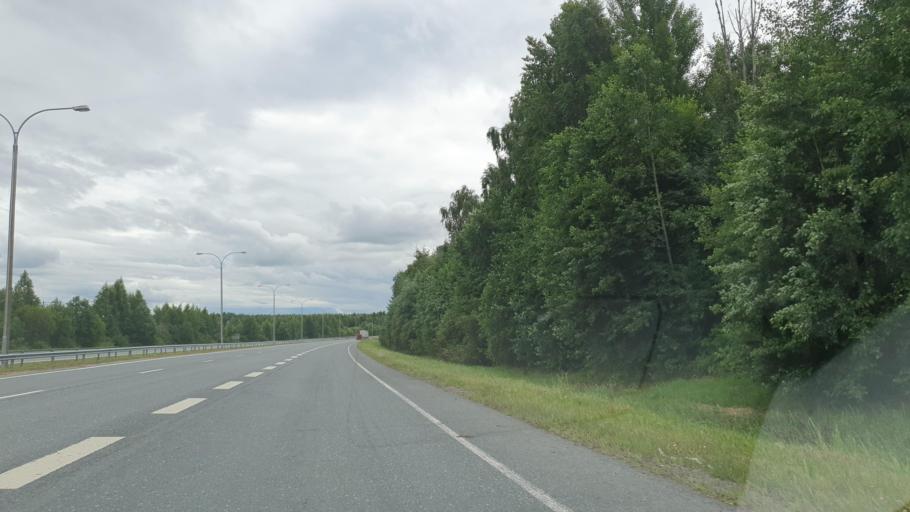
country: FI
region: Northern Savo
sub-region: Ylae-Savo
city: Iisalmi
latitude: 63.5223
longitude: 27.2512
